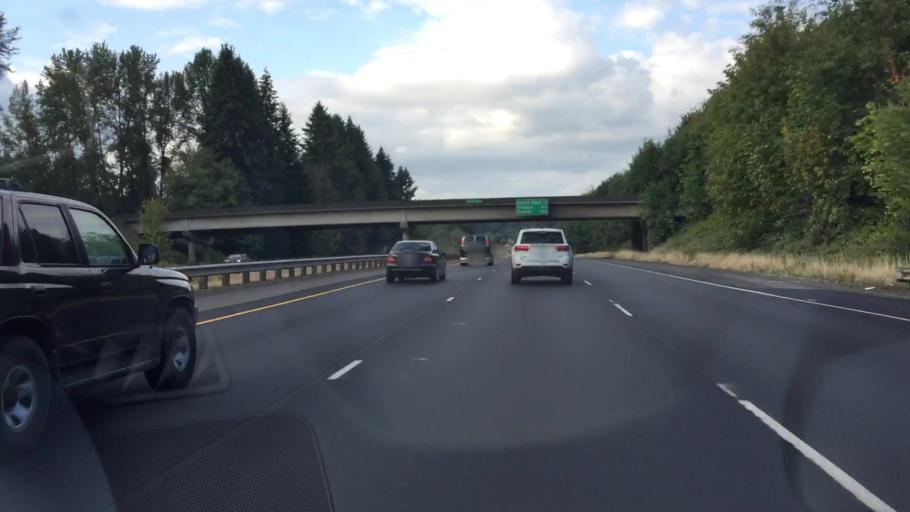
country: US
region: Washington
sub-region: Cowlitz County
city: West Side Highway
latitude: 46.1907
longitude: -122.8952
